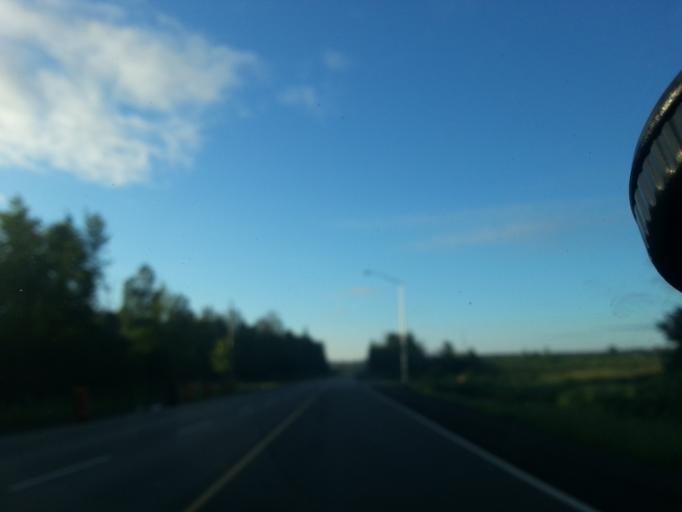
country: CA
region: Ontario
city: Carleton Place
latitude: 45.2671
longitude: -76.1258
